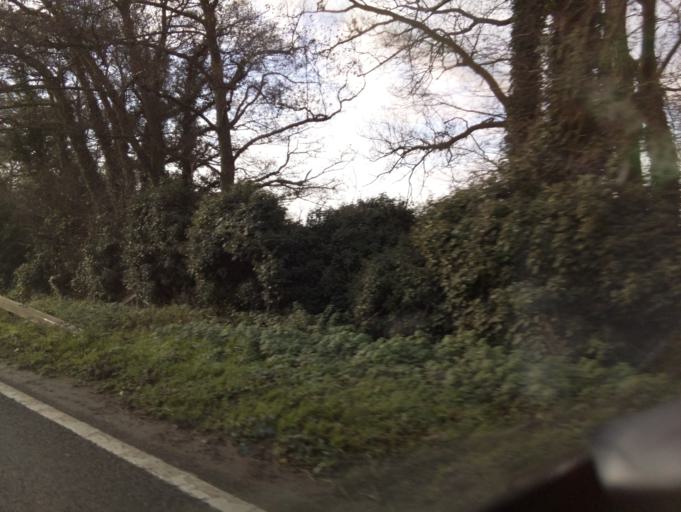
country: GB
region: England
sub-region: Warwickshire
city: Curdworth
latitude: 52.5708
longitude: -1.7636
